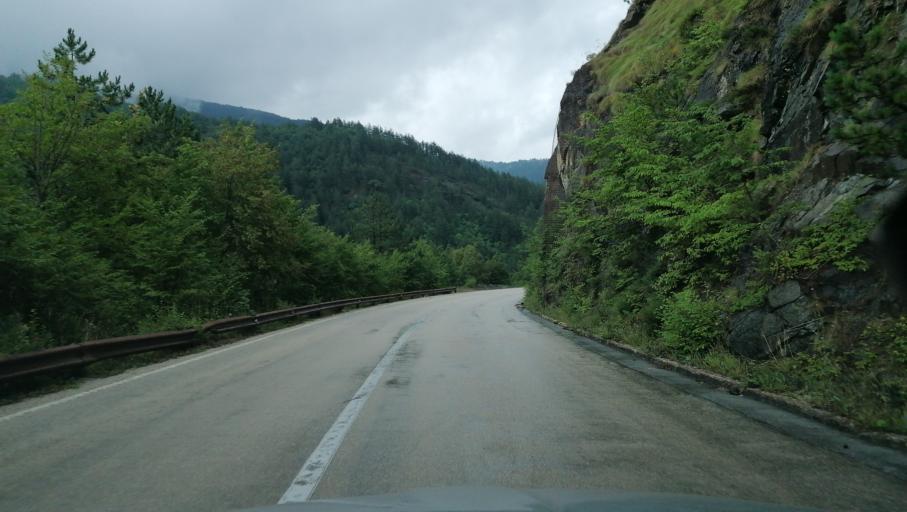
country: RS
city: Durici
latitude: 43.8139
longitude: 19.5144
